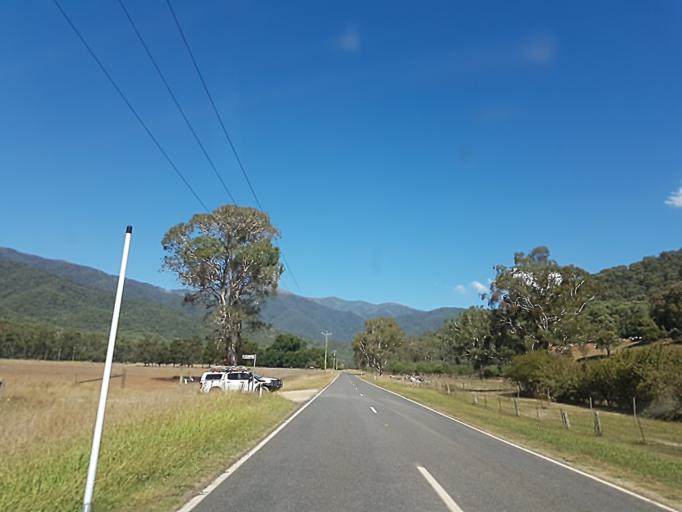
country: AU
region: Victoria
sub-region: Alpine
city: Mount Beauty
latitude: -36.8276
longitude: 147.0705
